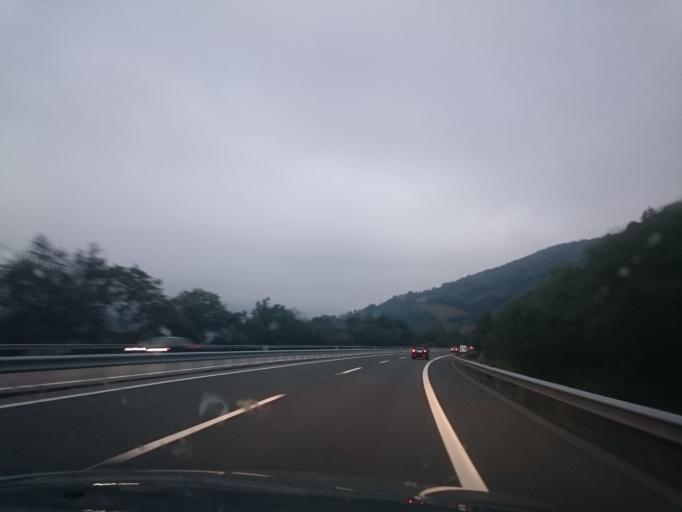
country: ES
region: Asturias
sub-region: Province of Asturias
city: Pola de Lena
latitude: 43.0489
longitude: -5.8211
